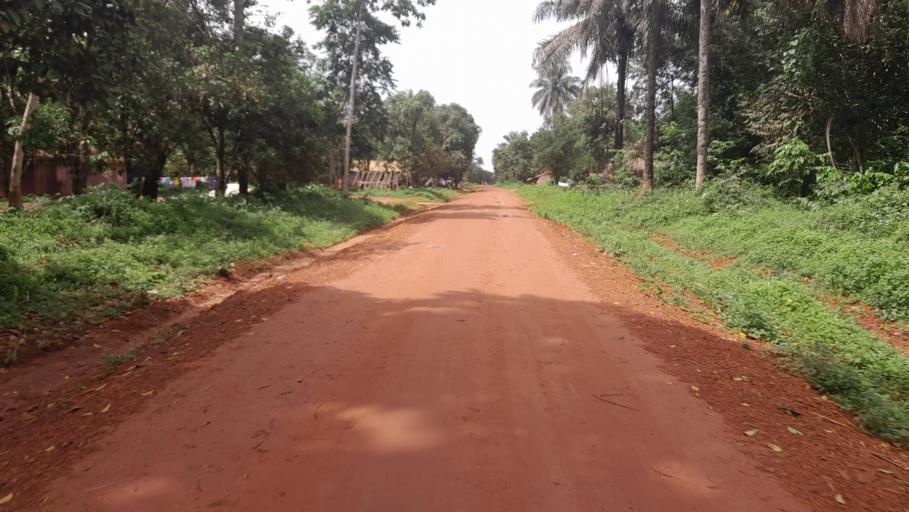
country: GN
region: Boke
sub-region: Boffa
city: Boffa
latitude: 10.0165
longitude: -13.8886
